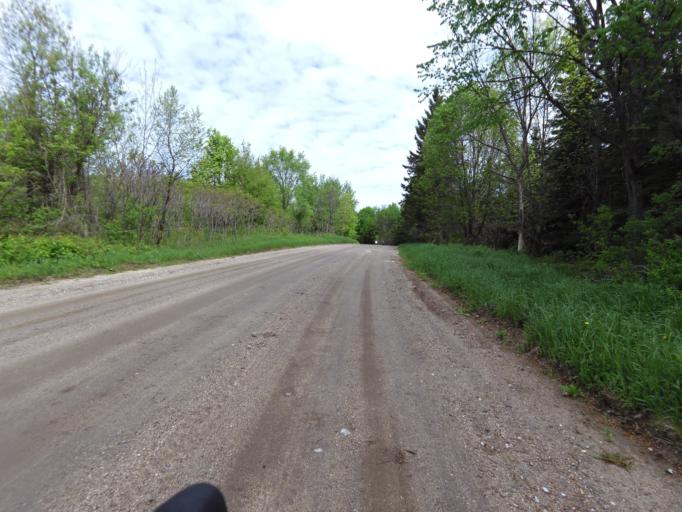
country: CA
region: Quebec
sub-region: Outaouais
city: Wakefield
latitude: 45.7629
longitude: -75.9168
